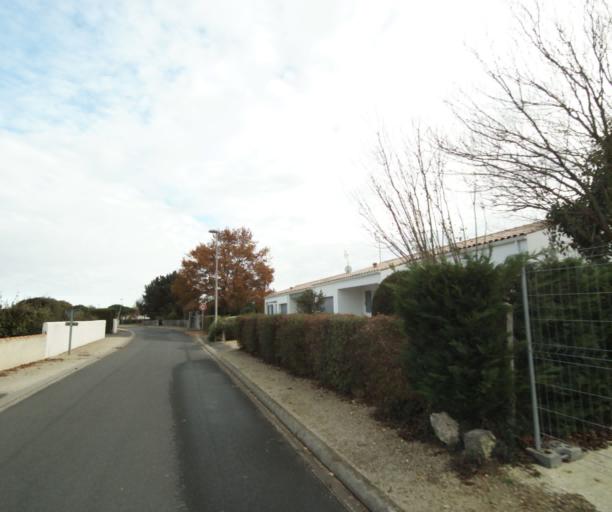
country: FR
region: Poitou-Charentes
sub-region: Departement de la Charente-Maritime
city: Corme-Royal
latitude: 45.7494
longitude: -0.8113
